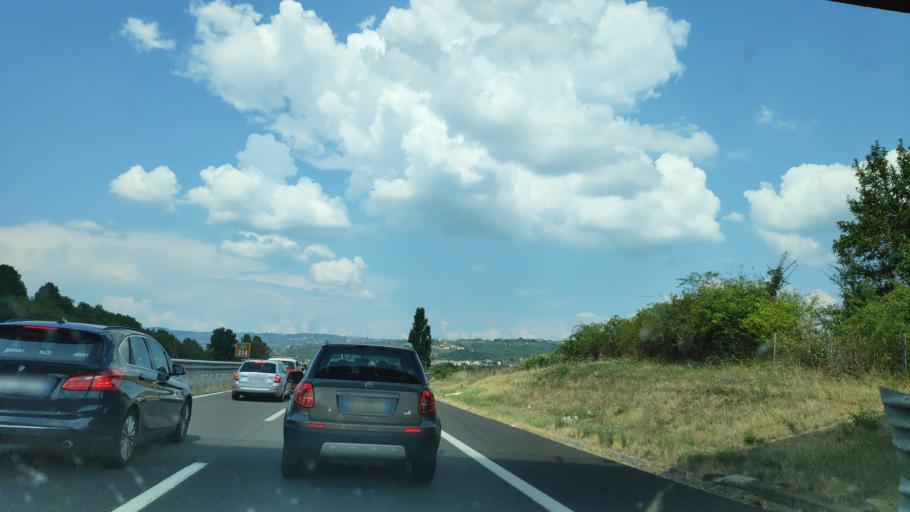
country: IT
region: Umbria
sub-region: Provincia di Terni
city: Fabro Scalo
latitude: 42.8562
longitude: 12.0381
